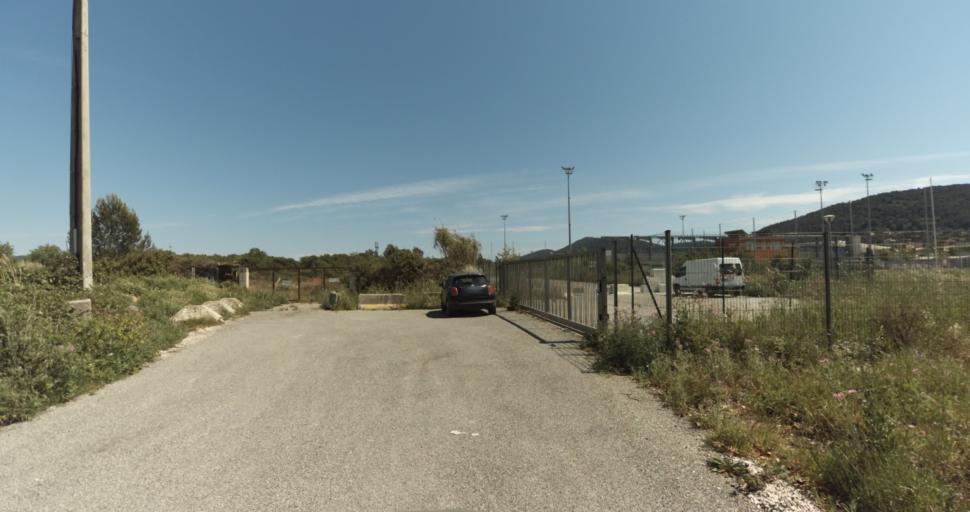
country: FR
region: Provence-Alpes-Cote d'Azur
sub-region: Departement du Var
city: La Crau
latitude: 43.1239
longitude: 6.0762
